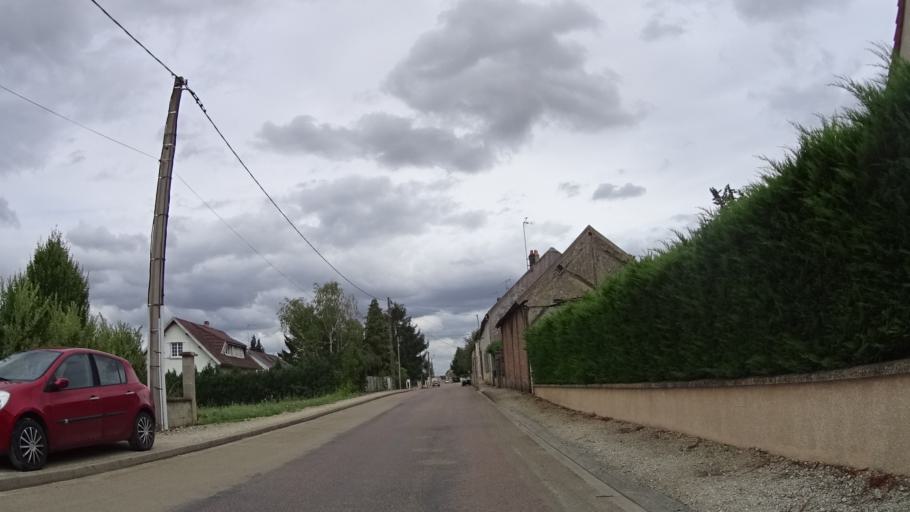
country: FR
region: Bourgogne
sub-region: Departement de l'Yonne
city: Joigny
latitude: 47.9532
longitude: 3.4088
